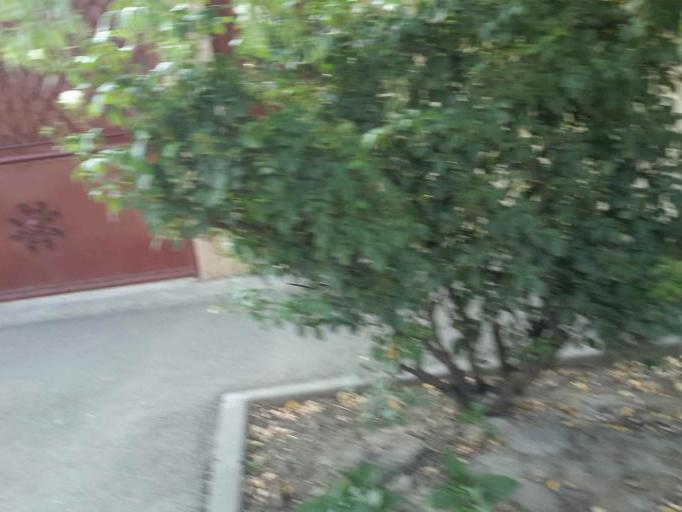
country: RO
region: Cluj
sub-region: Municipiul Cluj-Napoca
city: Cluj-Napoca
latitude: 46.7835
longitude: 23.6088
